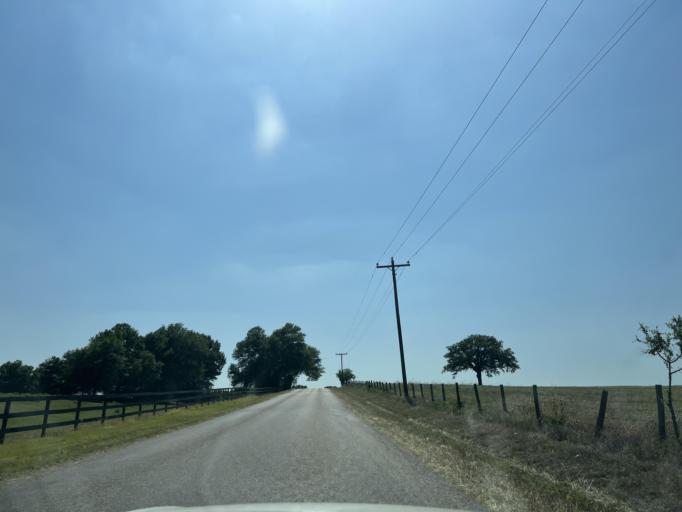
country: US
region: Texas
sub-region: Washington County
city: Brenham
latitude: 30.1604
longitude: -96.4415
